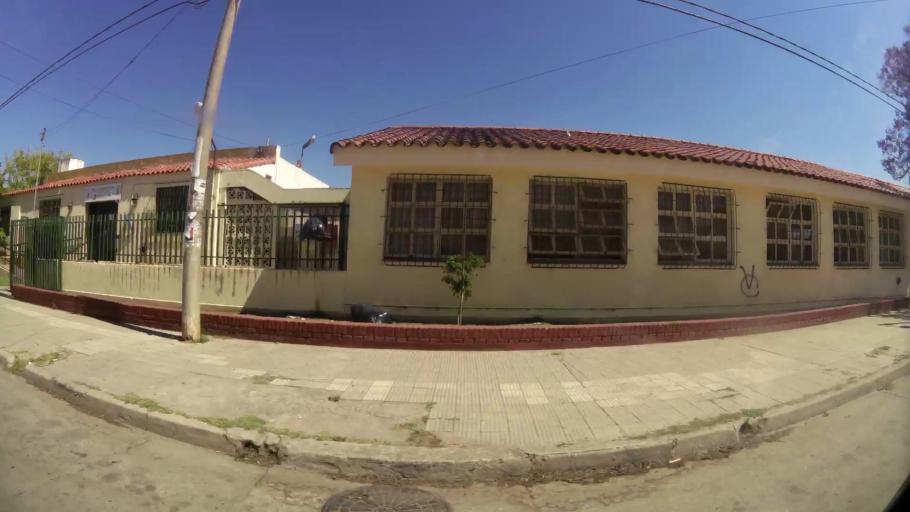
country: AR
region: Cordoba
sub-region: Departamento de Capital
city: Cordoba
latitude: -31.3777
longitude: -64.1409
